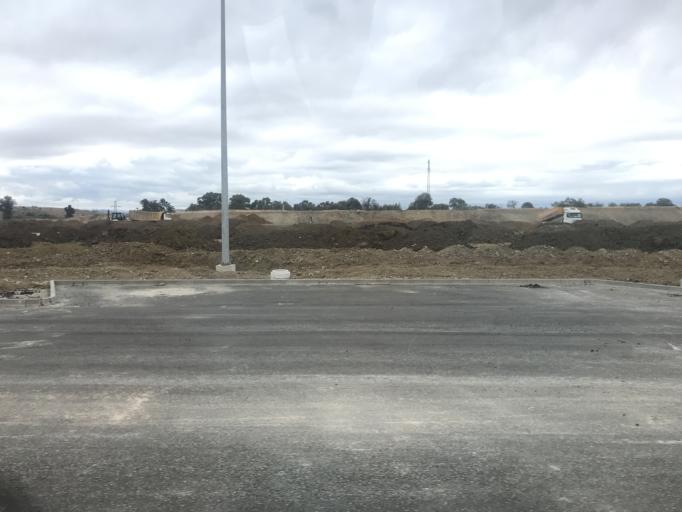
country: TR
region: Balikesir
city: Yenikoy
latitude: 39.7566
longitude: 27.9611
